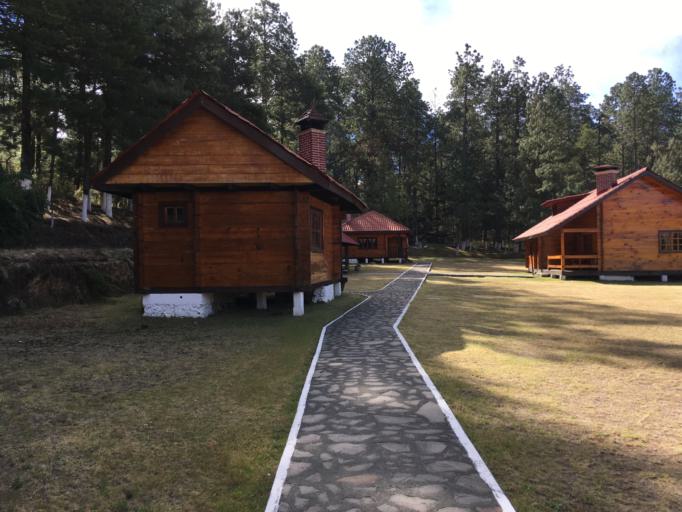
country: MX
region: Michoacan
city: Angahuan
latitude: 19.4946
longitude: -102.1989
